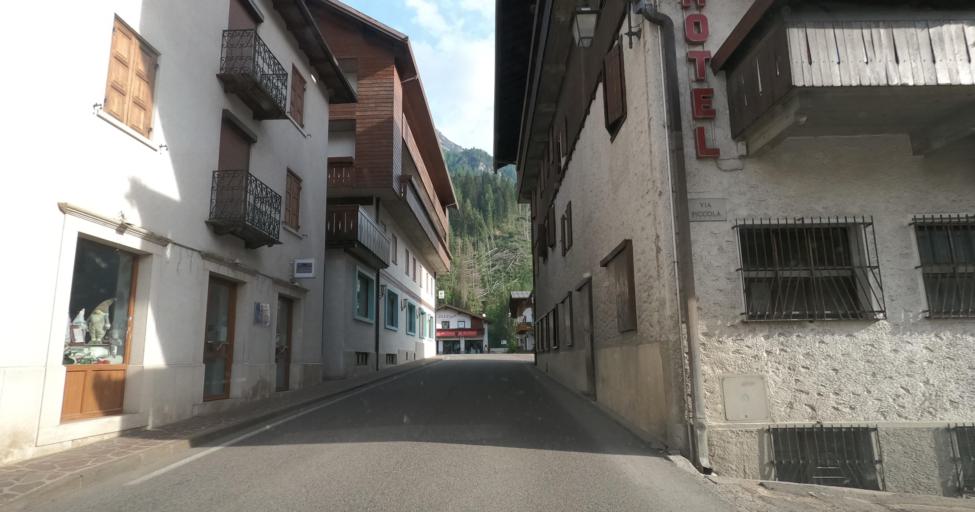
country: IT
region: Veneto
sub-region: Provincia di Belluno
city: Alleghe
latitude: 46.4066
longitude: 12.0205
